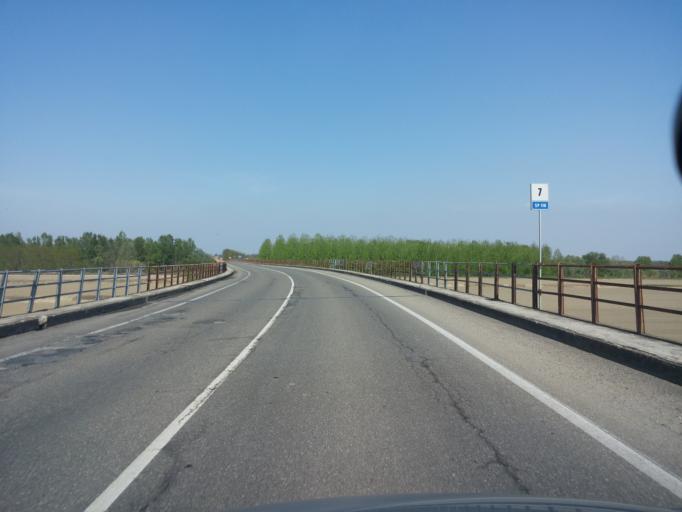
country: IT
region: Lombardy
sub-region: Provincia di Pavia
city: Langosco
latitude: 45.2054
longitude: 8.5418
